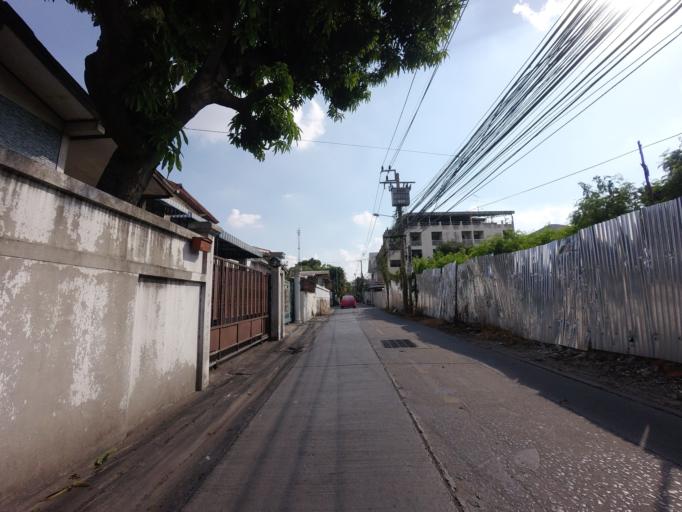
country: TH
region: Bangkok
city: Phaya Thai
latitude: 13.7939
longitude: 100.5551
